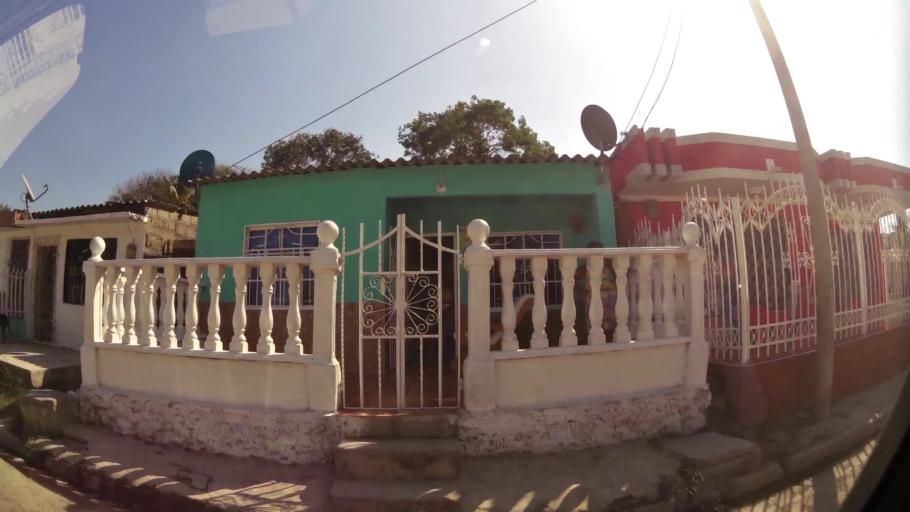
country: CO
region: Bolivar
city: Cartagena
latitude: 10.4106
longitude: -75.5131
